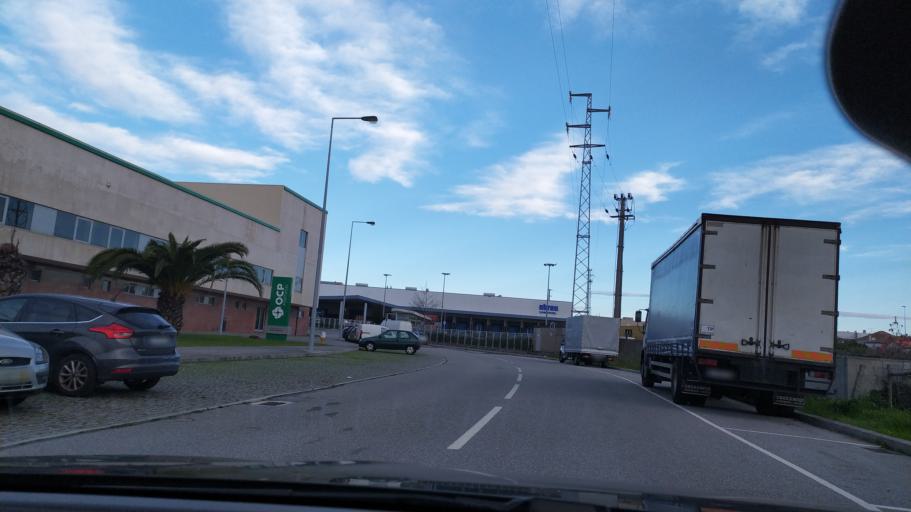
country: PT
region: Porto
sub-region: Matosinhos
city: Santa Cruz do Bispo
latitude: 41.2338
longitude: -8.6629
